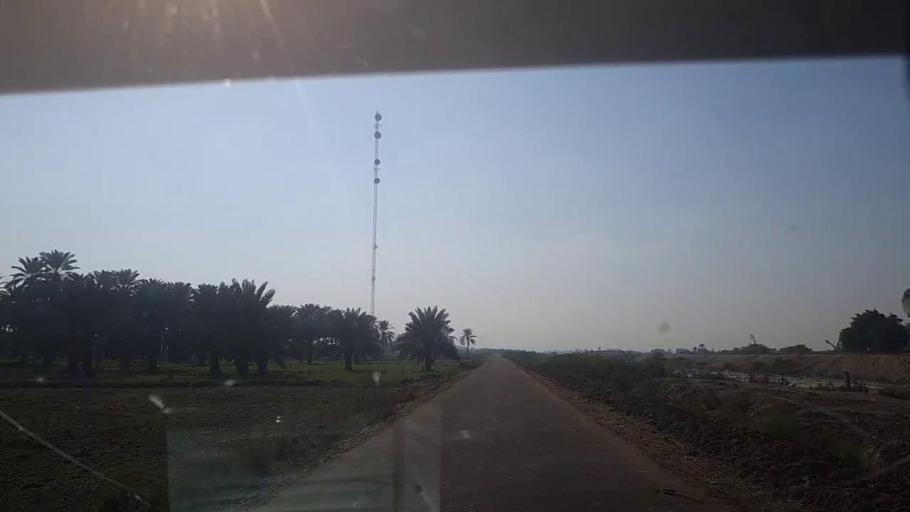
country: PK
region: Sindh
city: Gambat
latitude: 27.3856
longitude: 68.5909
